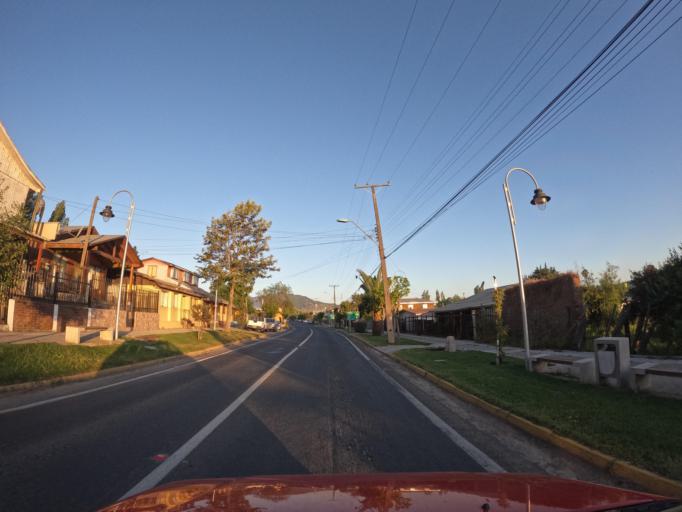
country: CL
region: Maule
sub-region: Provincia de Talca
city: Talca
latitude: -35.0896
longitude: -71.6616
